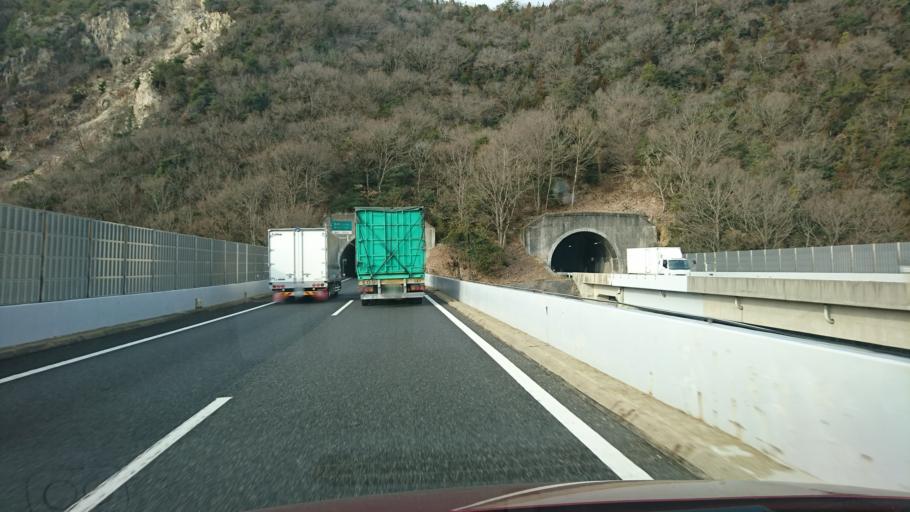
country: JP
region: Hyogo
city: Kariya
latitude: 34.7909
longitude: 134.4110
